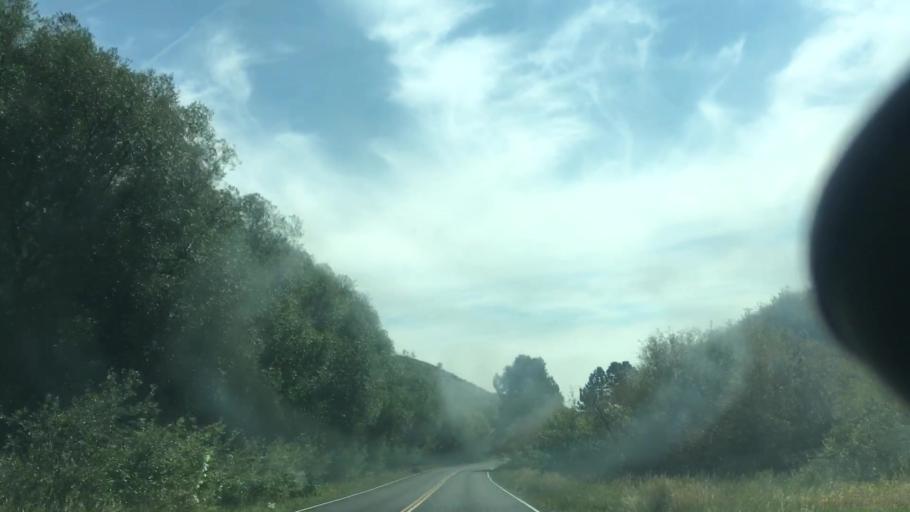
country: US
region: Colorado
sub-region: Larimer County
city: Laporte
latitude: 40.5423
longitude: -105.2823
